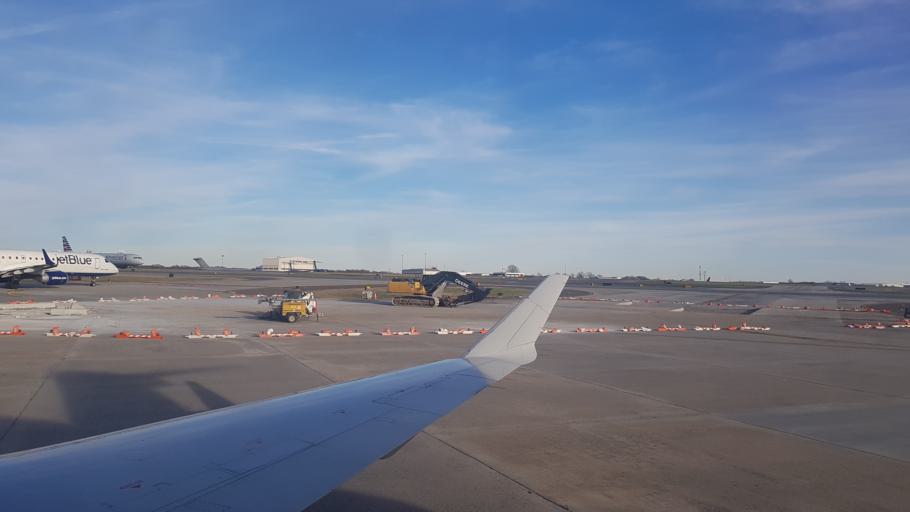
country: US
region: North Carolina
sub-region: Mecklenburg County
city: Charlotte
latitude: 35.2176
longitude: -80.9407
